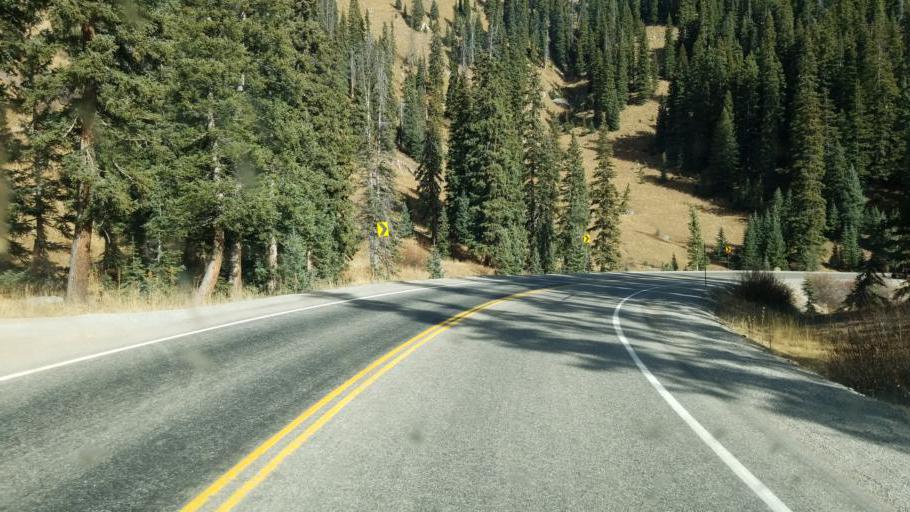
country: US
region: Colorado
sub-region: San Juan County
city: Silverton
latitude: 37.6998
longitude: -107.7779
